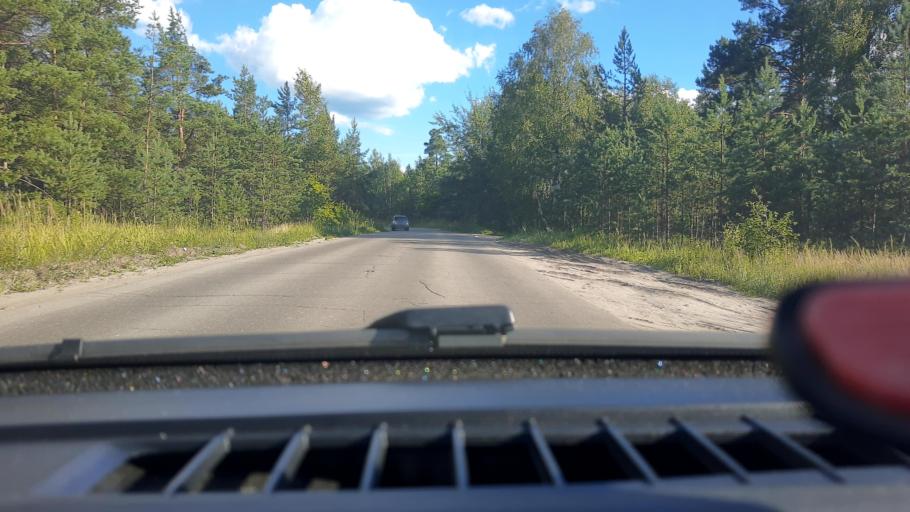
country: RU
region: Nizjnij Novgorod
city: Babino
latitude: 56.3097
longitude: 43.6303
